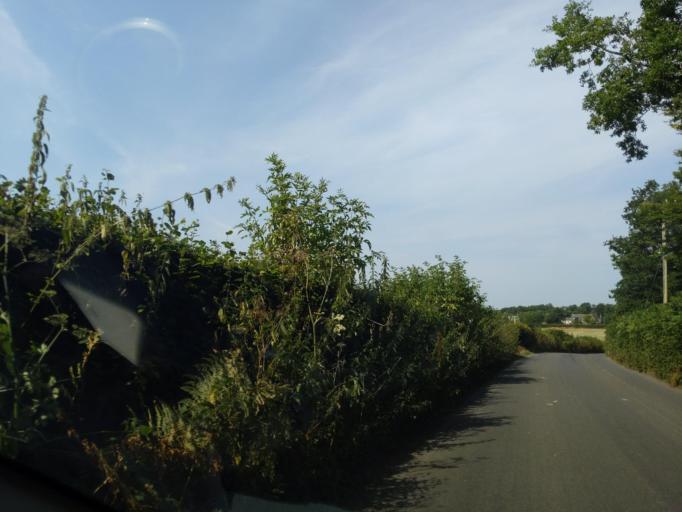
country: GB
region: England
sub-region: Devon
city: Winkleigh
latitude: 50.8795
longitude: -3.8932
